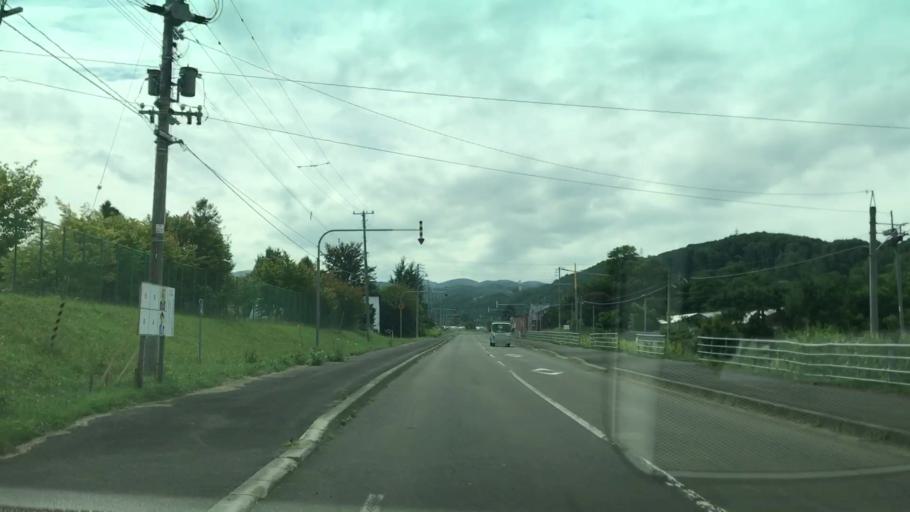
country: JP
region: Hokkaido
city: Yoichi
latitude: 43.1819
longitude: 140.8450
